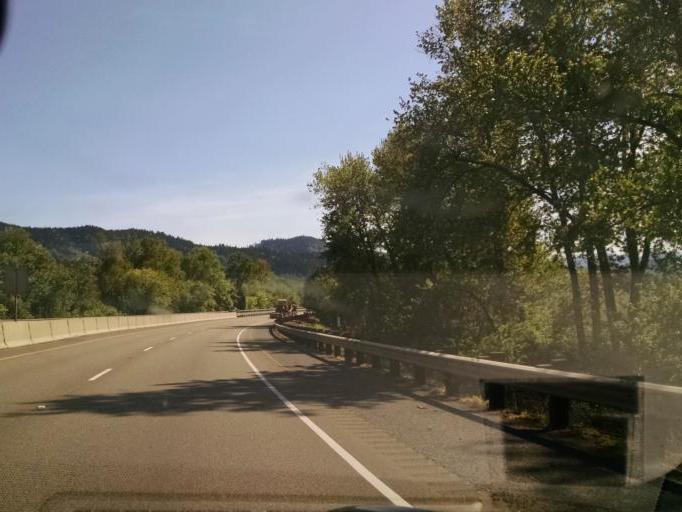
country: US
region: Oregon
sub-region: Douglas County
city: Myrtle Creek
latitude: 43.0146
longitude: -123.3006
